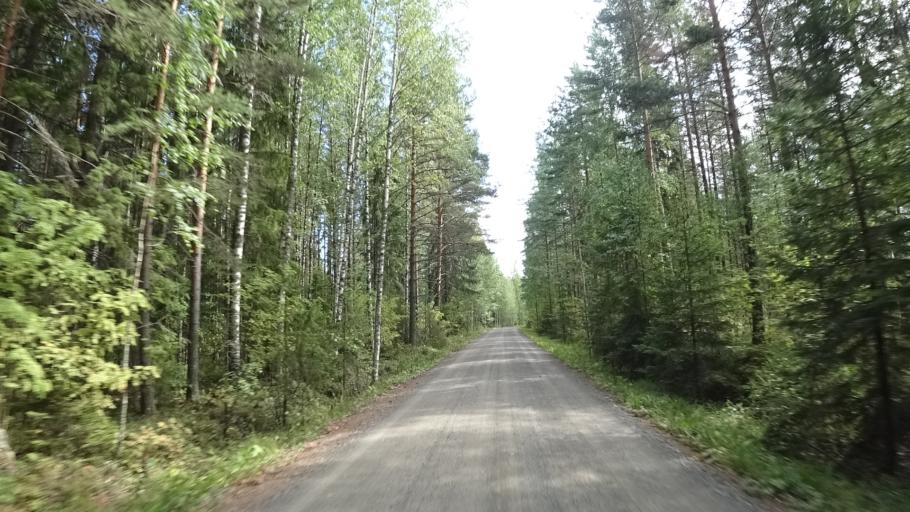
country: FI
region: North Karelia
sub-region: Joensuu
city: Pyhaeselkae
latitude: 62.3862
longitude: 29.7965
